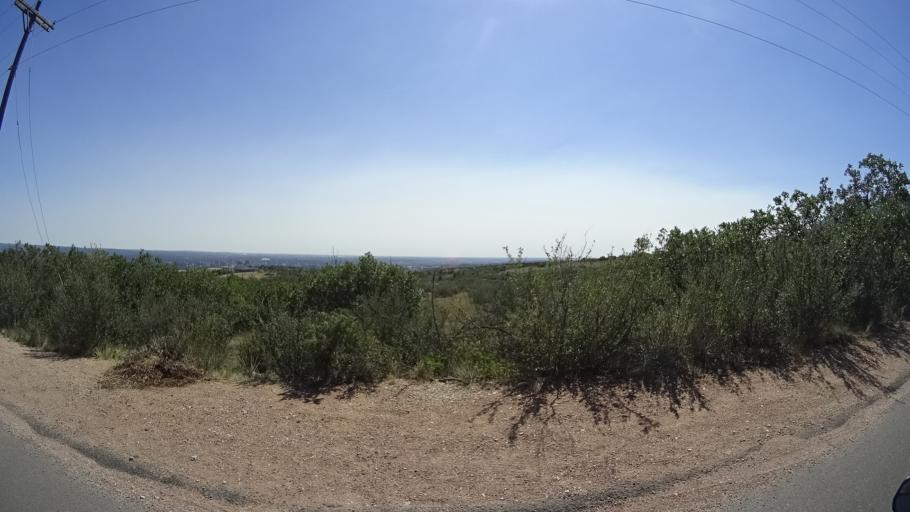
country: US
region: Colorado
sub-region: El Paso County
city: Manitou Springs
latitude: 38.8298
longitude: -104.8817
